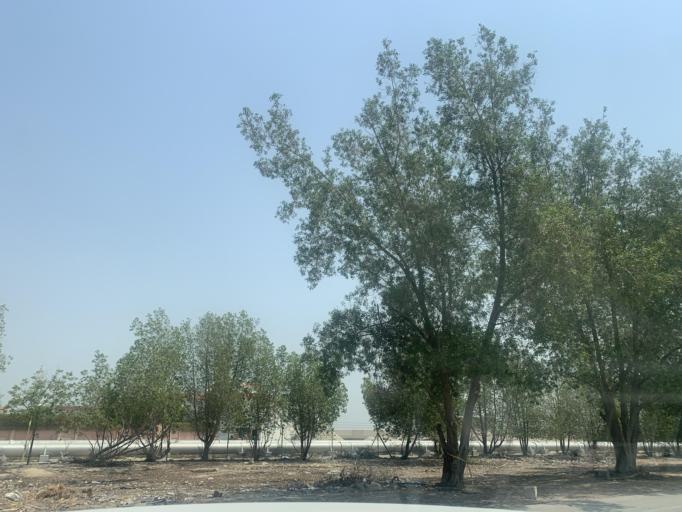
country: BH
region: Central Governorate
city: Madinat Hamad
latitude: 26.1432
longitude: 50.4784
